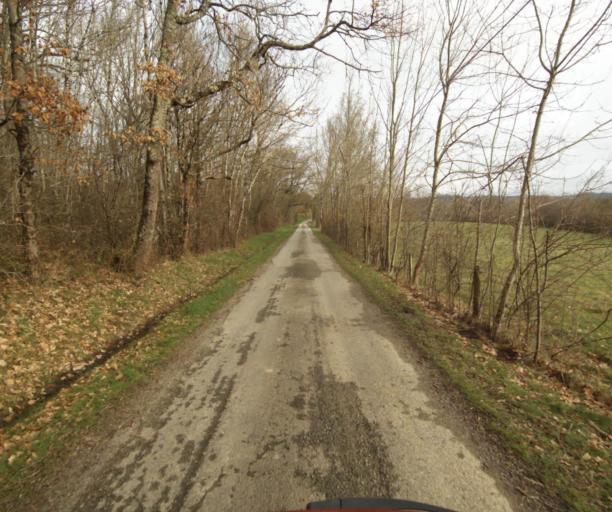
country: FR
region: Midi-Pyrenees
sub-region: Departement de la Haute-Garonne
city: Gaillac-Toulza
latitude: 43.1630
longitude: 1.4859
